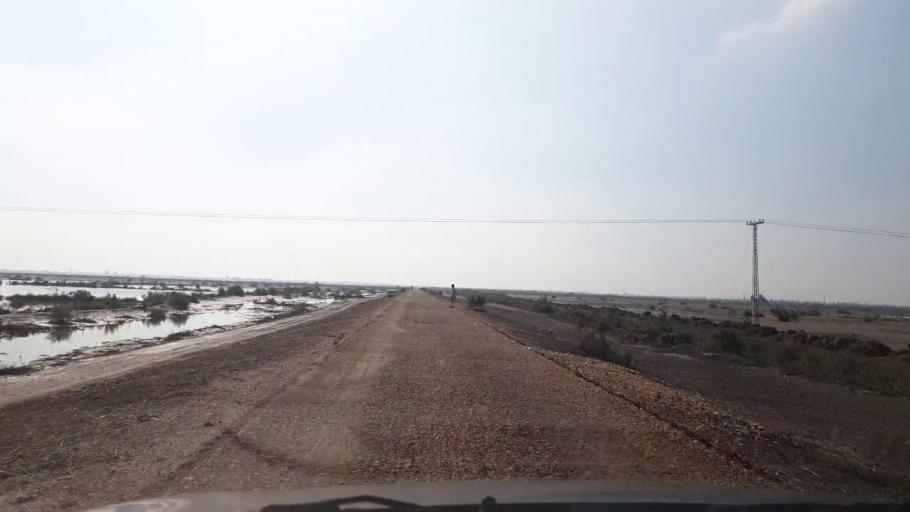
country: PK
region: Sindh
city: Sinjhoro
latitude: 26.0357
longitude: 68.7787
